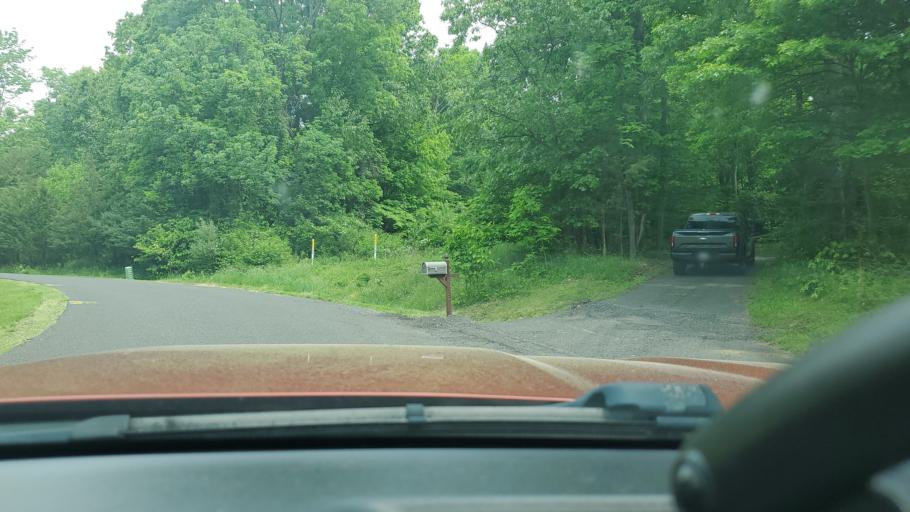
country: US
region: Pennsylvania
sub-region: Montgomery County
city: Red Hill
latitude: 40.3391
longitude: -75.4936
